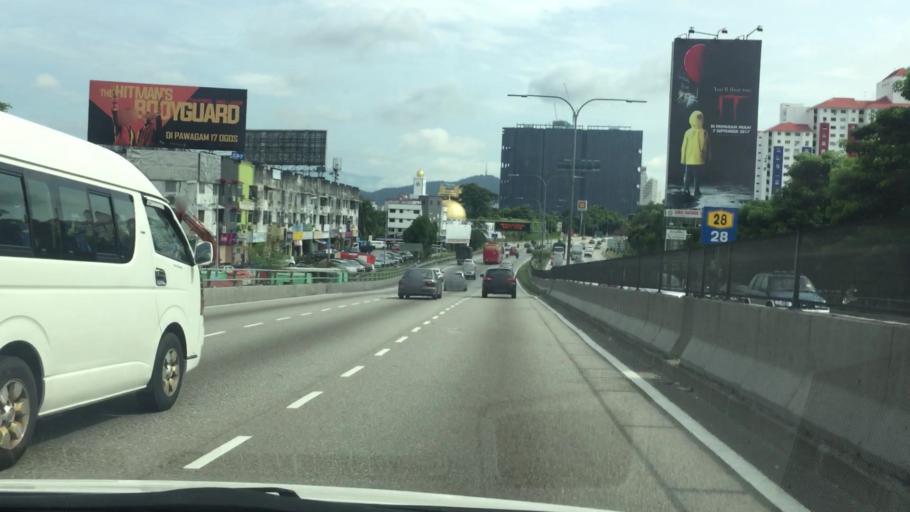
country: MY
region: Kuala Lumpur
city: Kuala Lumpur
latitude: 3.1474
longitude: 101.7444
